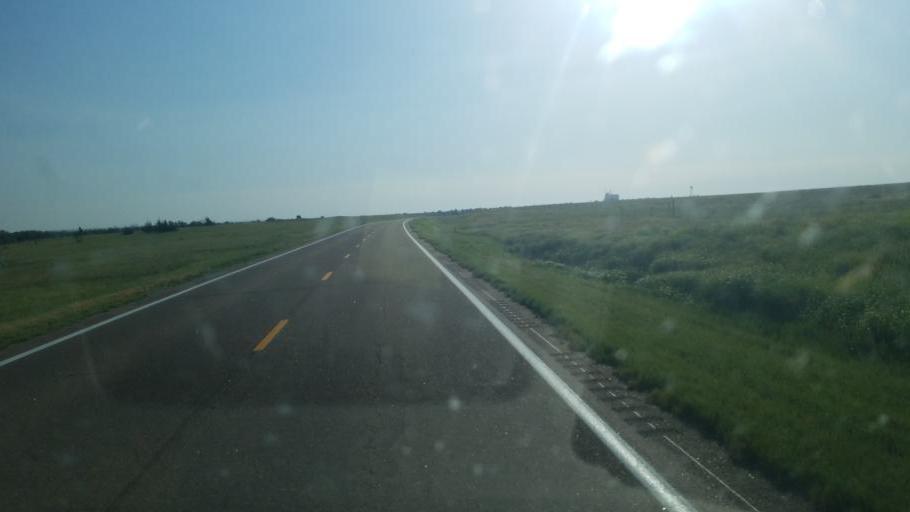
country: US
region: Kansas
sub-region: Edwards County
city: Kinsley
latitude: 38.1855
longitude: -99.5552
